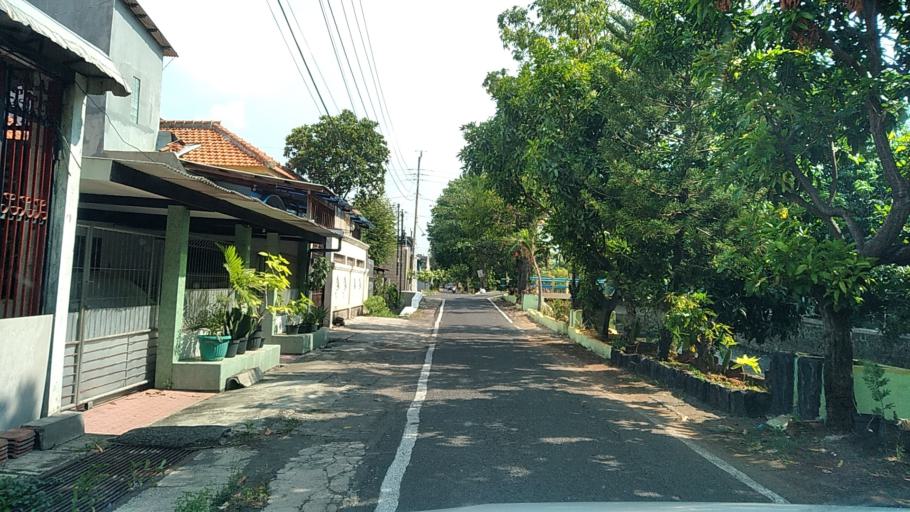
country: ID
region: Central Java
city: Semarang
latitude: -6.9795
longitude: 110.4374
